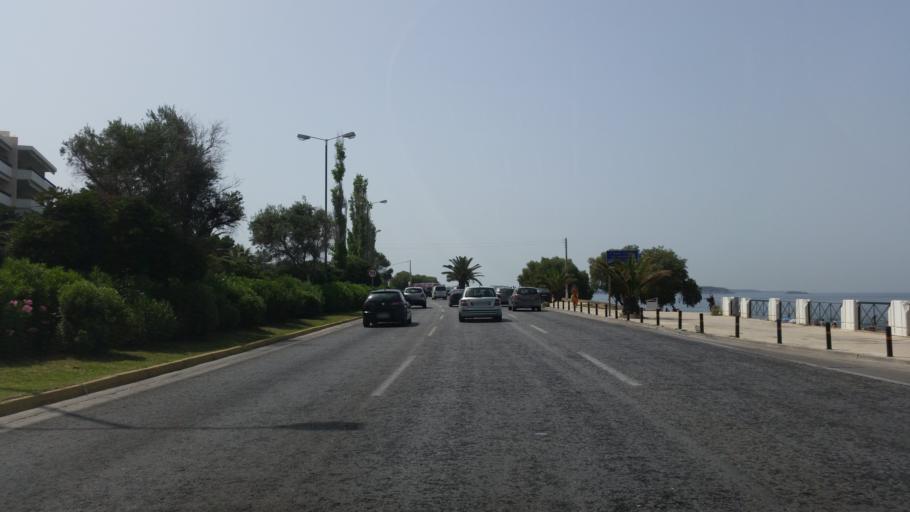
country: GR
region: Attica
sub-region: Nomarchia Athinas
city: Glyfada
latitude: 37.8470
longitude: 23.7537
